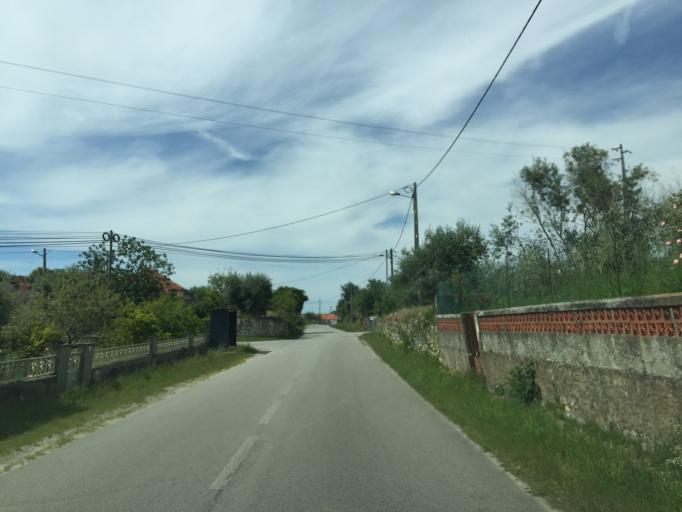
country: PT
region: Coimbra
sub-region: Soure
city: Soure
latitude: 40.0130
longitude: -8.5809
